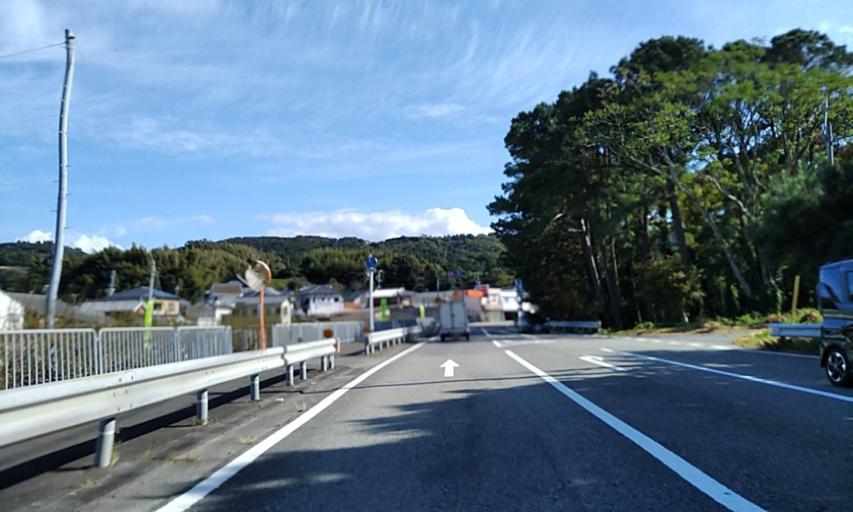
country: JP
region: Wakayama
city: Gobo
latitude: 33.7976
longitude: 135.2391
